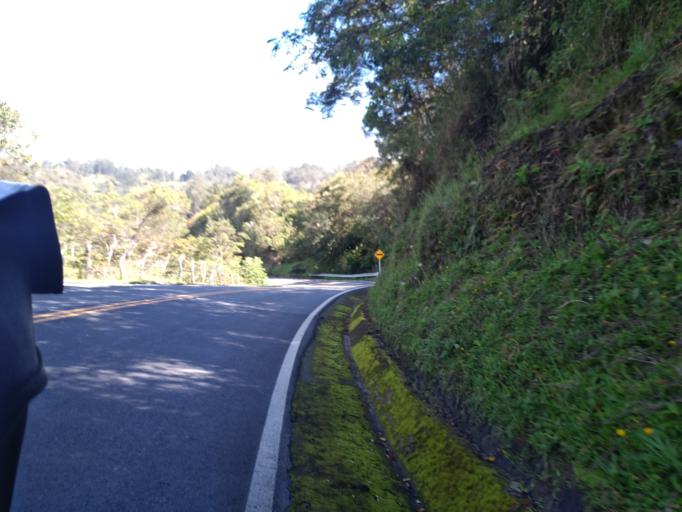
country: CO
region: Santander
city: Velez
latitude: 5.9994
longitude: -73.6903
